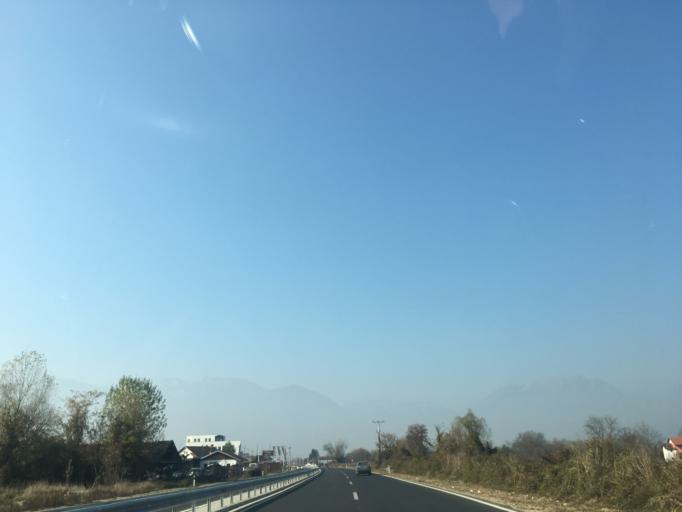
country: XK
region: Pec
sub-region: Komuna e Pejes
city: Dubova (Driloni)
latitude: 42.6596
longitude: 20.3655
